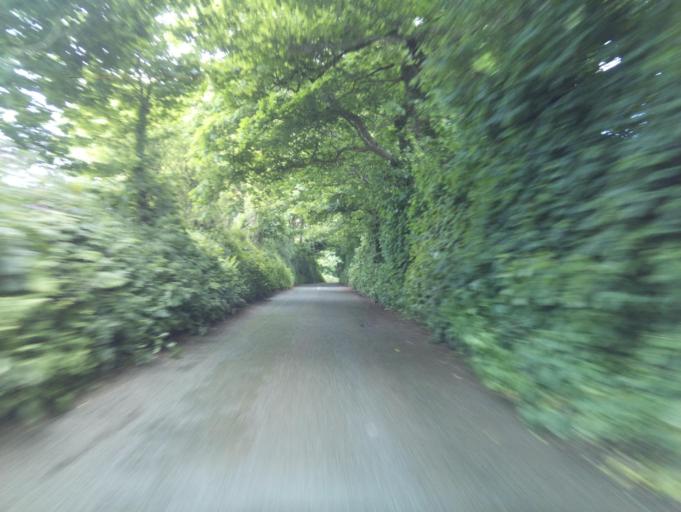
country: GB
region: England
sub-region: Devon
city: Dartmouth
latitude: 50.3571
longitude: -3.5455
